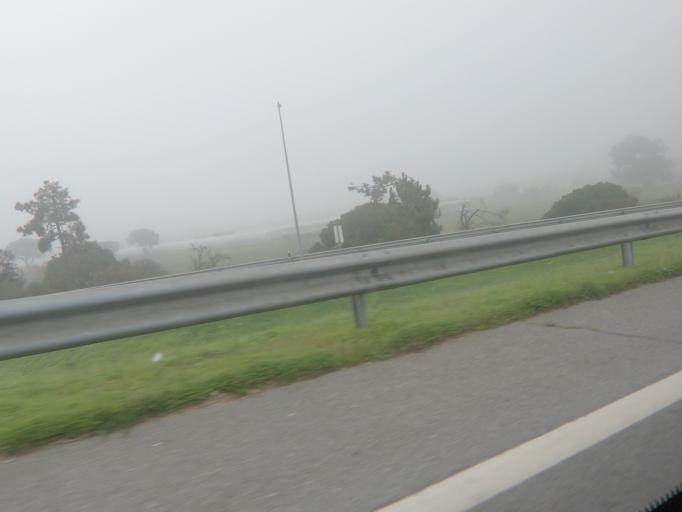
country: PT
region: Setubal
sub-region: Montijo
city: Montijo
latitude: 38.6793
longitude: -8.9457
